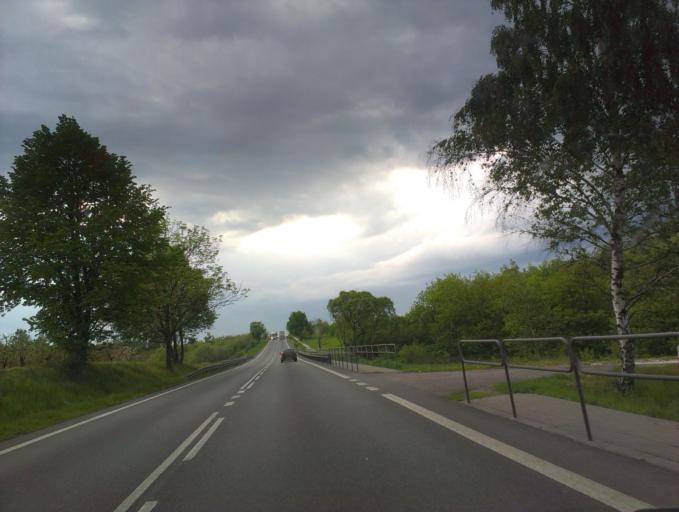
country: PL
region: Masovian Voivodeship
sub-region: Powiat grojecki
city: Pniewy
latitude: 51.8996
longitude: 20.7723
